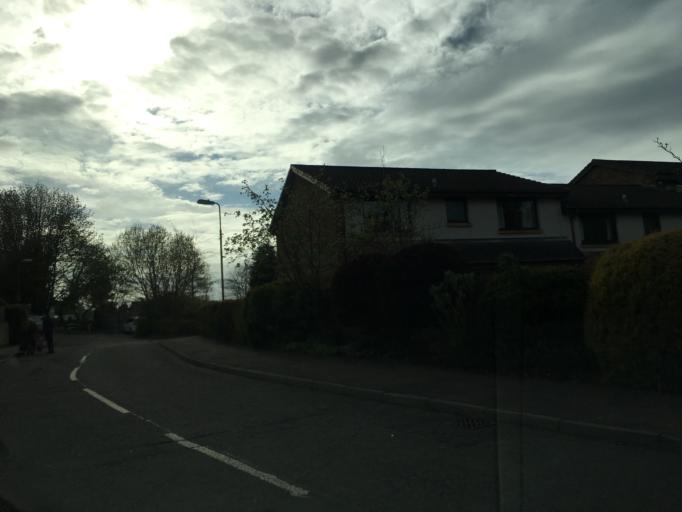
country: GB
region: Scotland
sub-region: Edinburgh
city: Colinton
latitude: 55.9065
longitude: -3.2176
